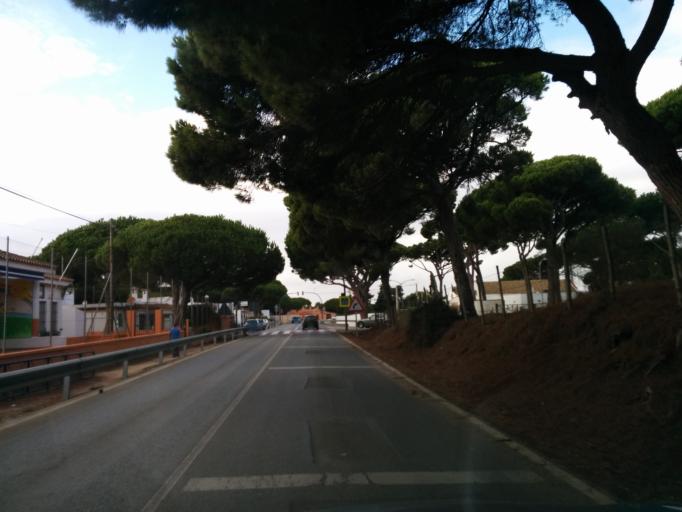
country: ES
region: Andalusia
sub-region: Provincia de Cadiz
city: Vejer de la Frontera
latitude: 36.2002
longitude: -6.0347
